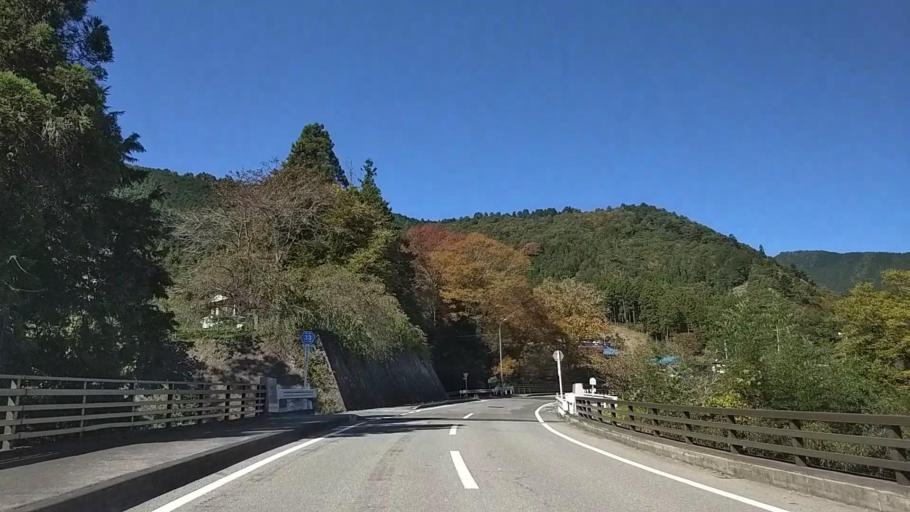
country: JP
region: Yamanashi
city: Uenohara
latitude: 35.6640
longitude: 139.0873
